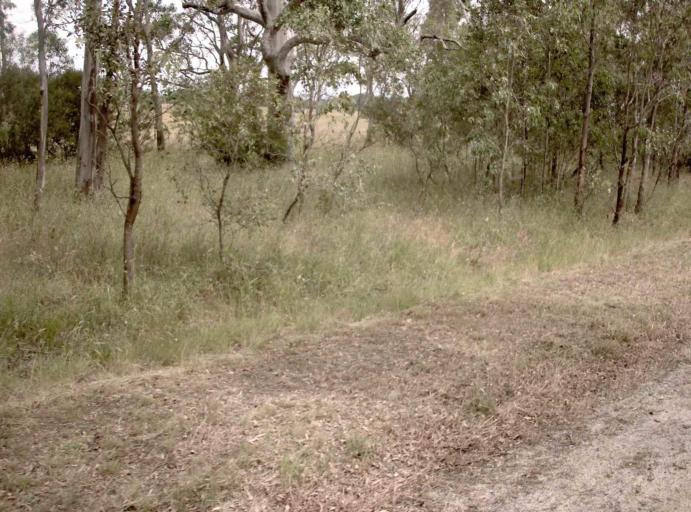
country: AU
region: Victoria
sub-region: Wellington
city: Sale
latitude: -37.9011
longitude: 147.0742
